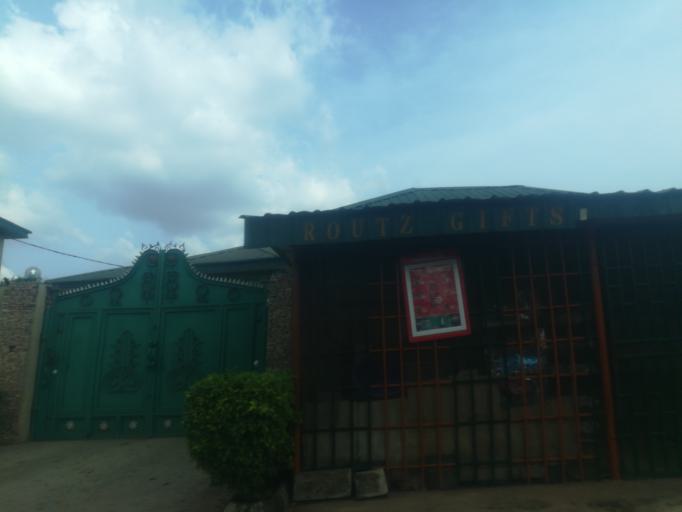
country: NG
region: Ogun
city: Abeokuta
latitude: 7.1271
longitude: 3.3206
